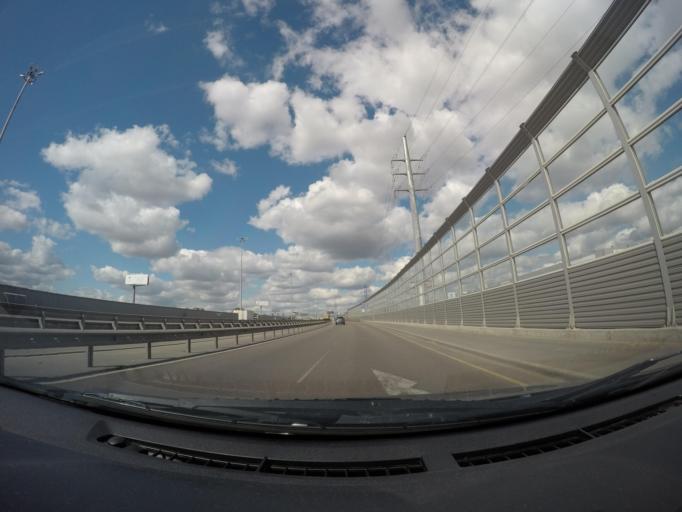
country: RU
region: Moskovskaya
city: Lyubertsy
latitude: 55.6540
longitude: 37.9031
